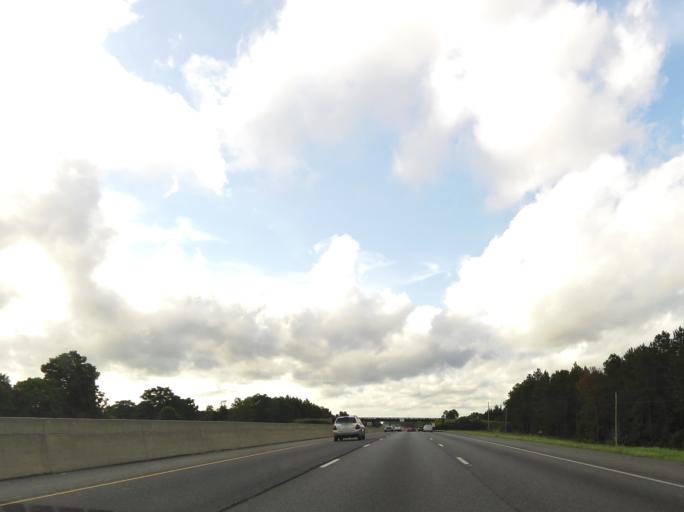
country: US
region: Georgia
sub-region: Crisp County
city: Cordele
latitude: 31.8489
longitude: -83.7173
